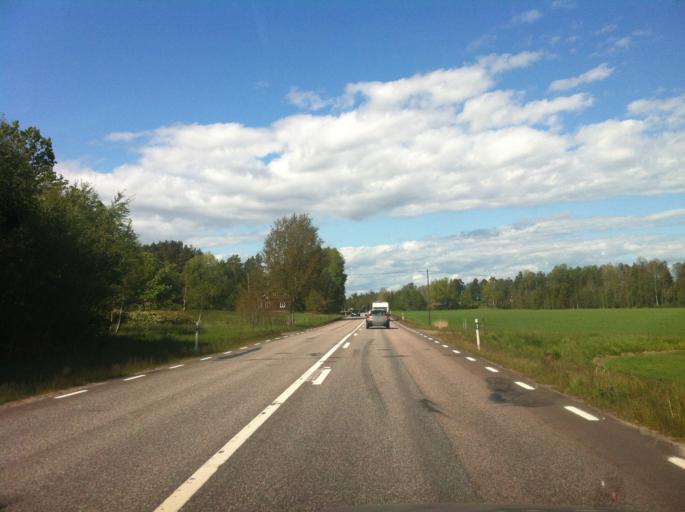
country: SE
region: Vaermland
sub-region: Kristinehamns Kommun
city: Bjorneborg
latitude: 59.1281
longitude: 14.1766
